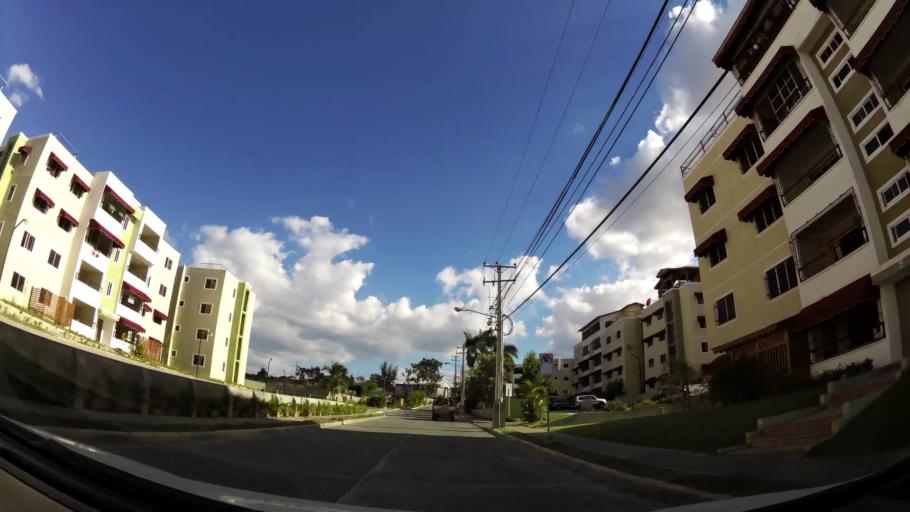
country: DO
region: Nacional
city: Santo Domingo
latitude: 18.5091
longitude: -69.9797
